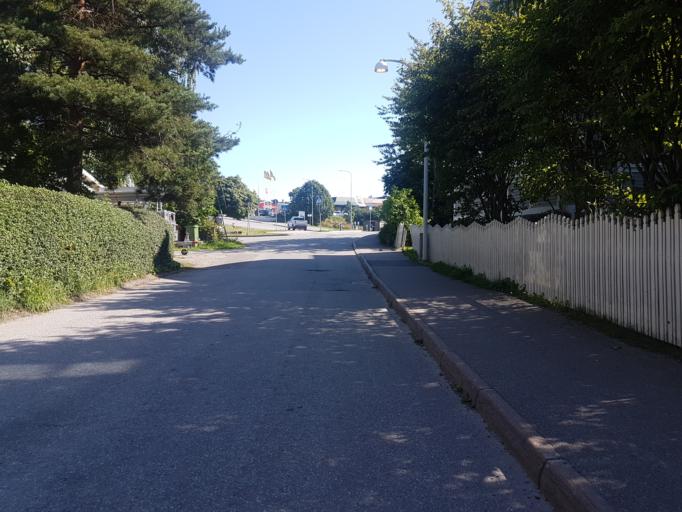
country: SE
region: Stockholm
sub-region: Nacka Kommun
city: Nacka
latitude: 59.3135
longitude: 18.1589
